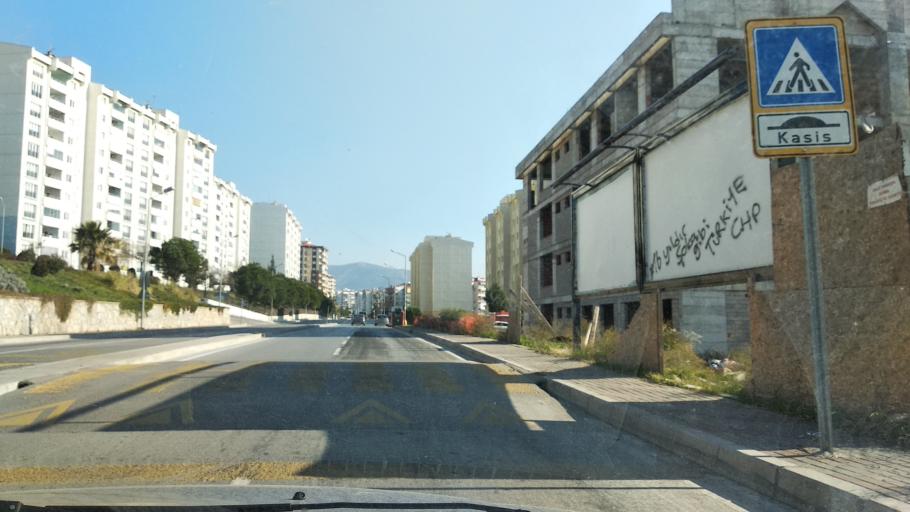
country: TR
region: Izmir
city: Karsiyaka
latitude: 38.4927
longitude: 27.0891
